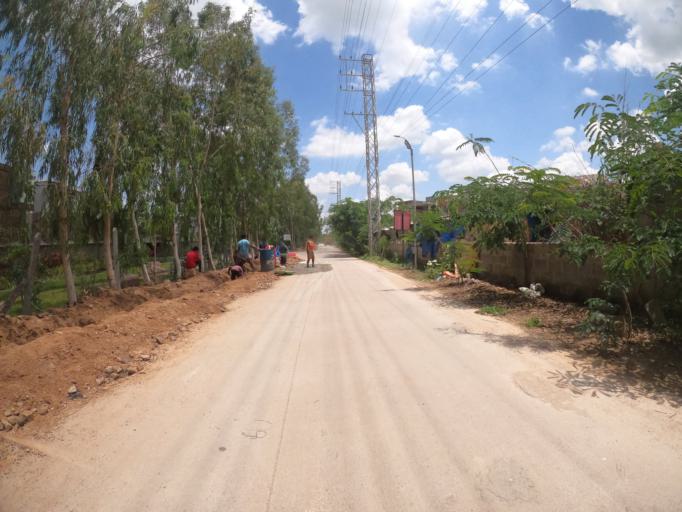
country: IN
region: Telangana
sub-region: Medak
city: Serilingampalle
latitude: 17.3831
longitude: 78.3252
